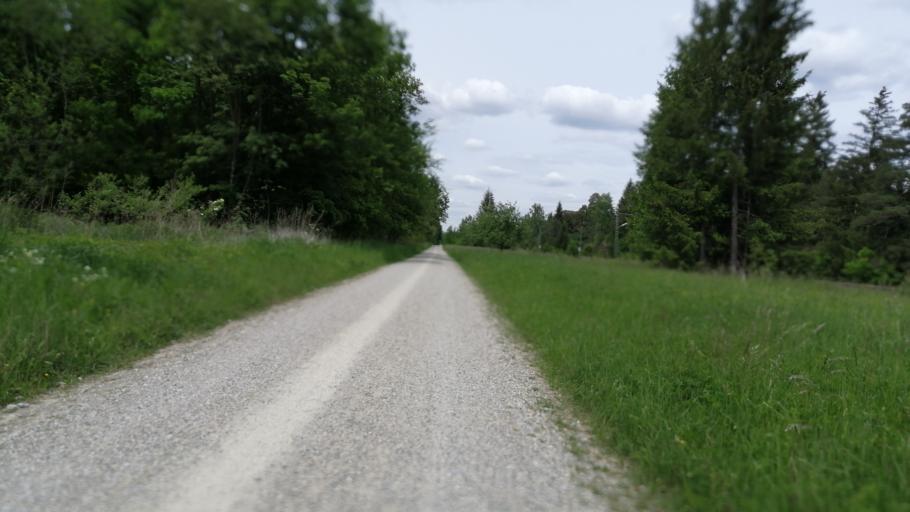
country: DE
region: Bavaria
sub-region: Upper Bavaria
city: Oberhaching
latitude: 48.0560
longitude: 11.5660
